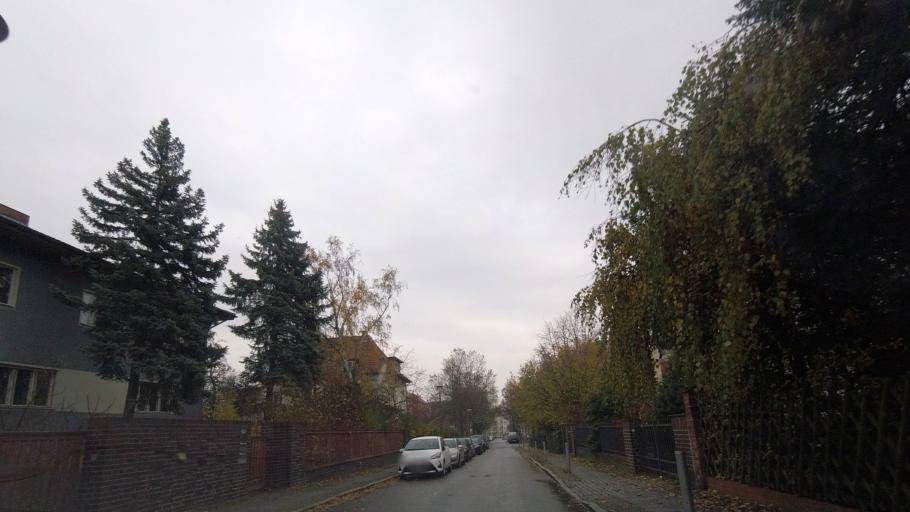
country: DE
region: Berlin
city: Weissensee
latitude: 52.5587
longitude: 13.4564
